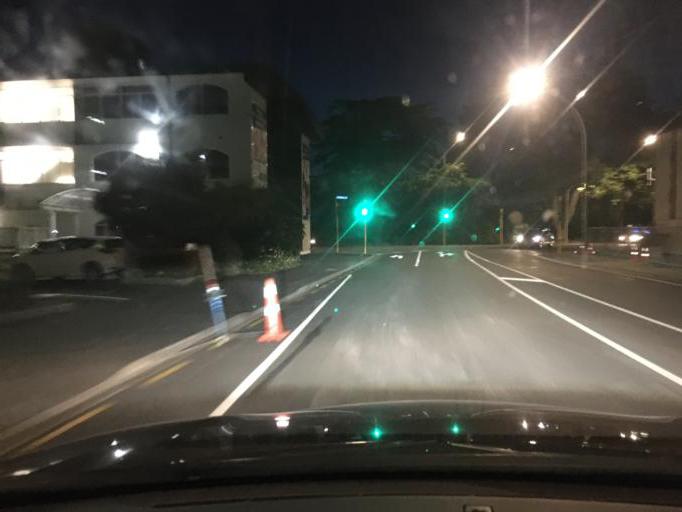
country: NZ
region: Waikato
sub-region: Hamilton City
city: Hamilton
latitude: -37.7855
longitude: 175.2754
